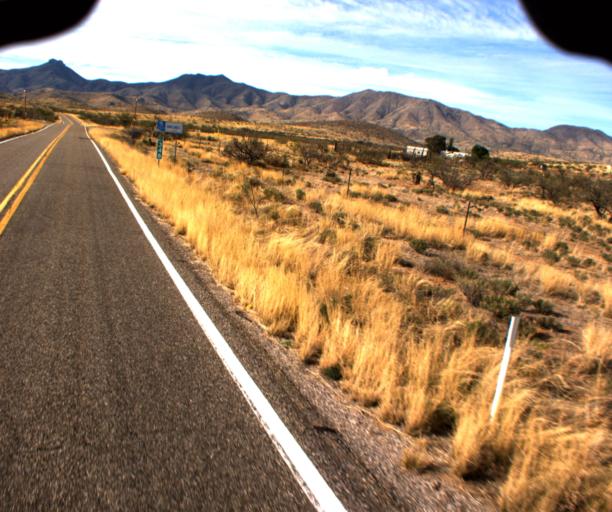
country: US
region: Arizona
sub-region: Cochise County
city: Willcox
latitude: 32.1295
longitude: -109.5576
